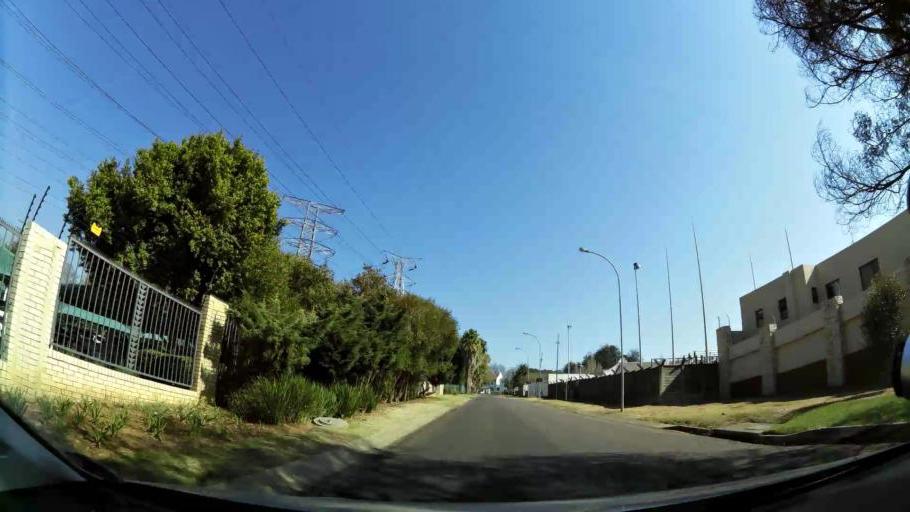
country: ZA
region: Gauteng
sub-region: City of Johannesburg Metropolitan Municipality
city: Modderfontein
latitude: -26.1612
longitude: 28.1303
